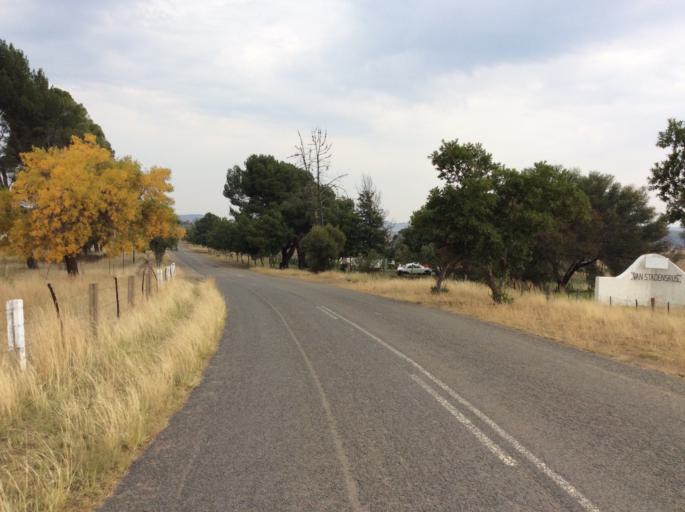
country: LS
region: Mafeteng
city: Mafeteng
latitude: -29.9862
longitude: 27.0189
